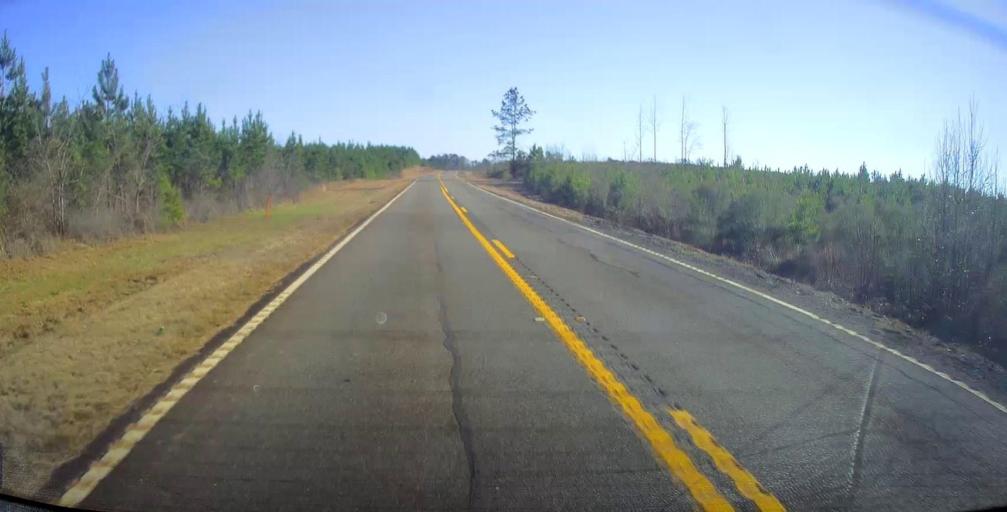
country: US
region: Georgia
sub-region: Talbot County
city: Talbotton
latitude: 32.6589
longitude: -84.4591
